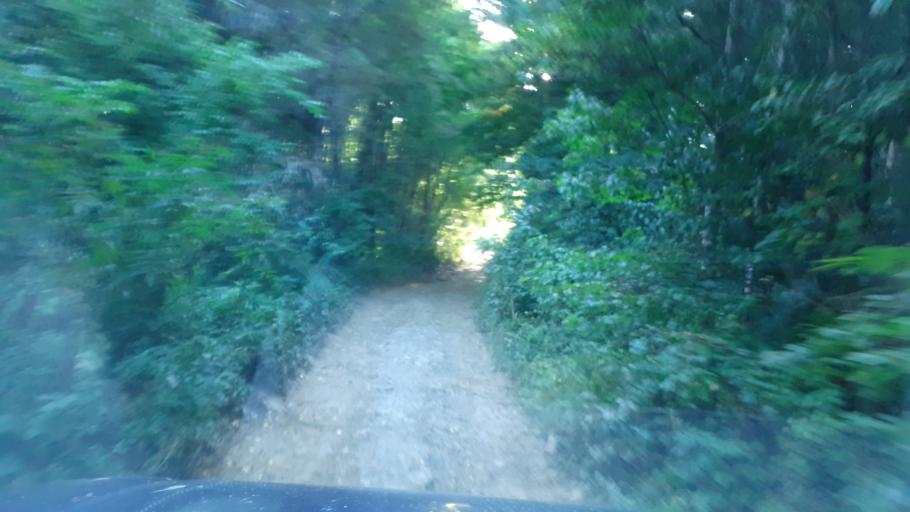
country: RU
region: Krasnodarskiy
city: Chernomorskiy
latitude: 44.6613
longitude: 38.4666
